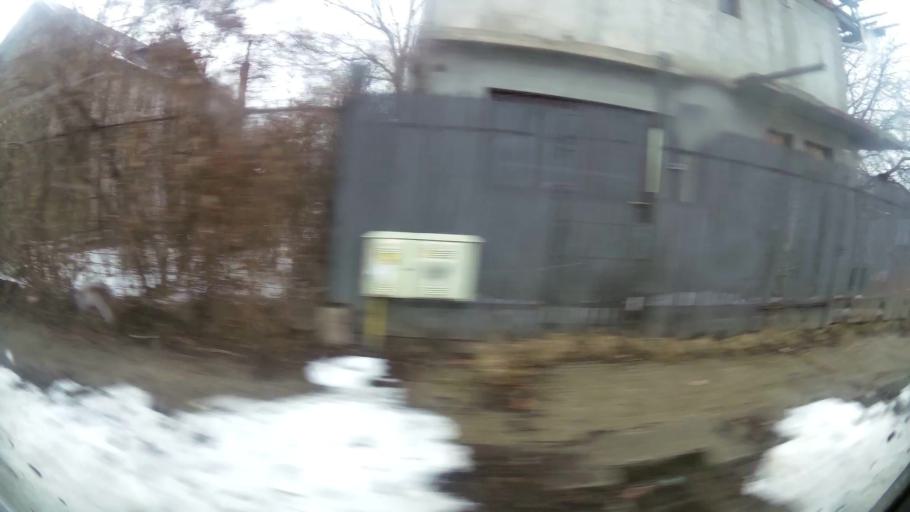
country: RO
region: Ilfov
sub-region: Comuna Chiajna
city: Rosu
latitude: 44.4284
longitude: 26.0127
